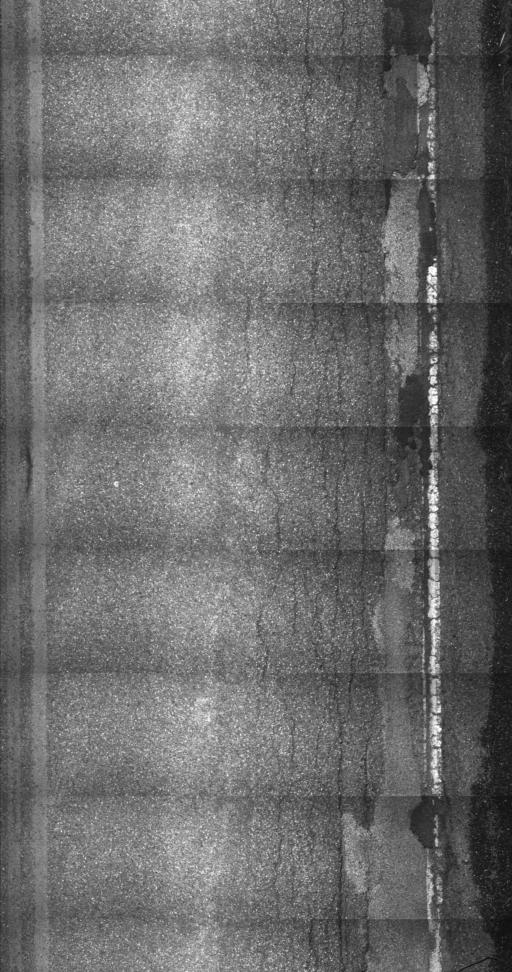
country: US
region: Vermont
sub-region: Bennington County
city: Manchester Center
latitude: 43.2656
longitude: -73.1065
